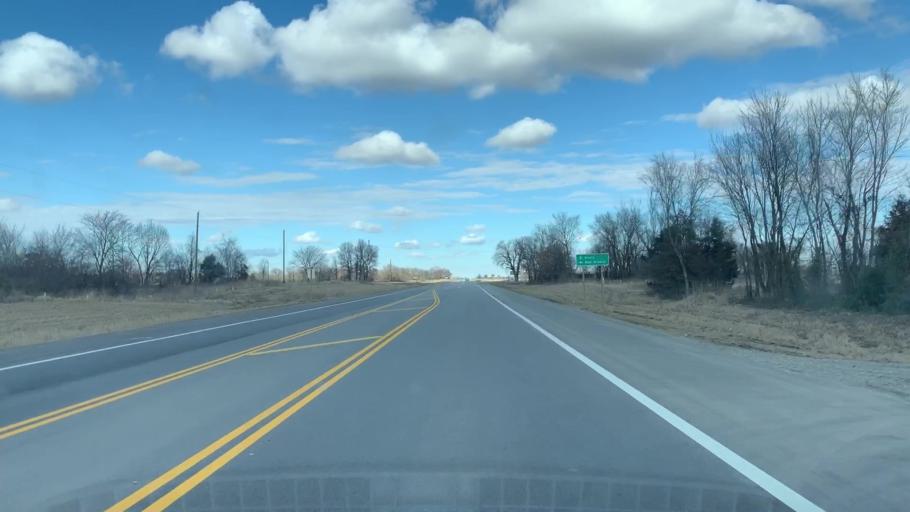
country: US
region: Kansas
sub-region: Cherokee County
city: Columbus
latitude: 37.2784
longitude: -94.8321
